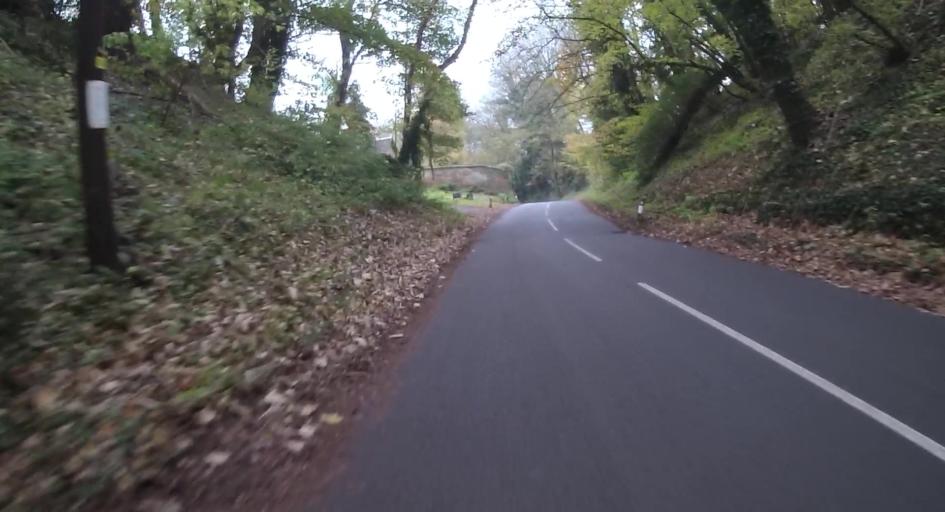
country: GB
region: England
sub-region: Hampshire
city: Kingsley
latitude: 51.1639
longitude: -0.8746
